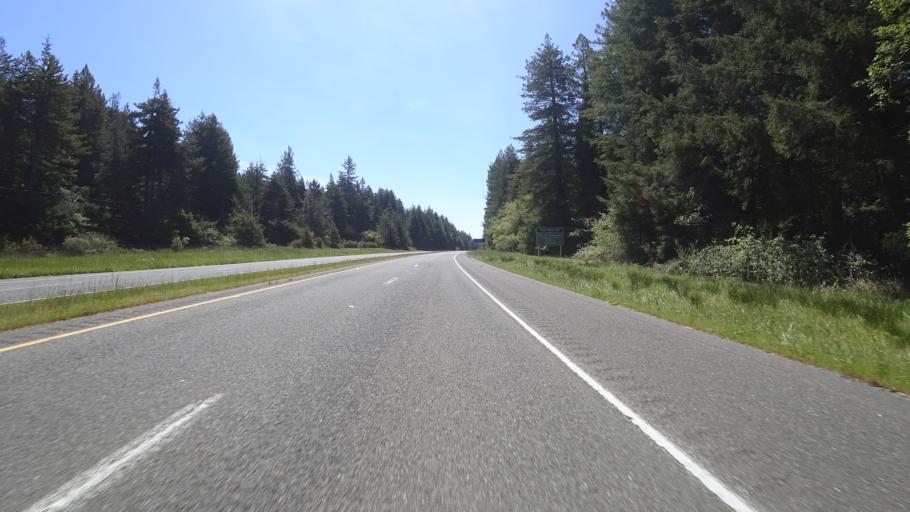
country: US
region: California
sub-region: Humboldt County
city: Westhaven-Moonstone
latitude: 41.0736
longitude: -124.1415
